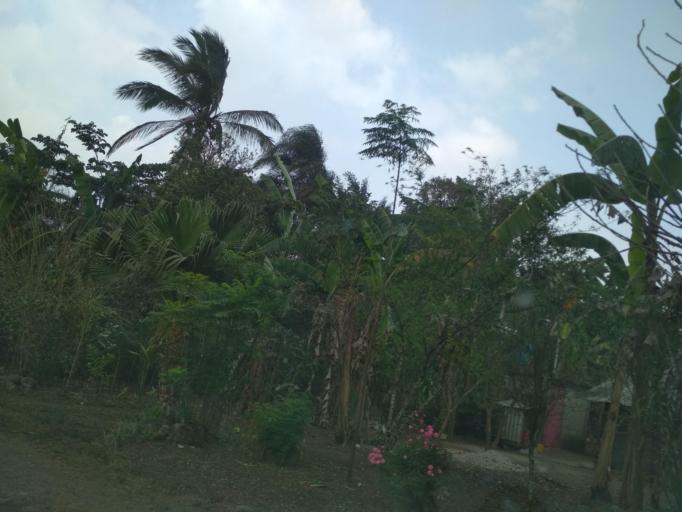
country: MX
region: Veracruz
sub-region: Cordoba
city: San Jose de Tapia
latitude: 18.8353
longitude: -96.9792
